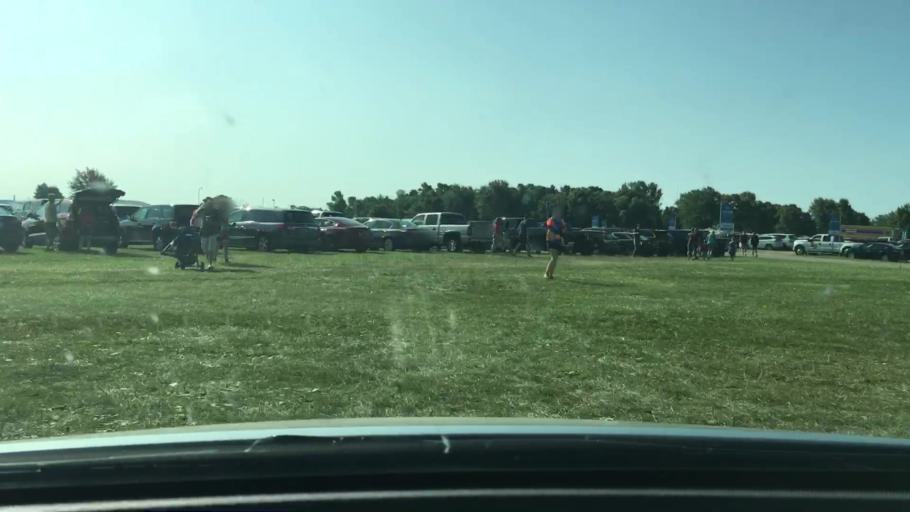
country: US
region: Wisconsin
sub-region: Winnebago County
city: Oshkosh
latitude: 43.9805
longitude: -88.5711
